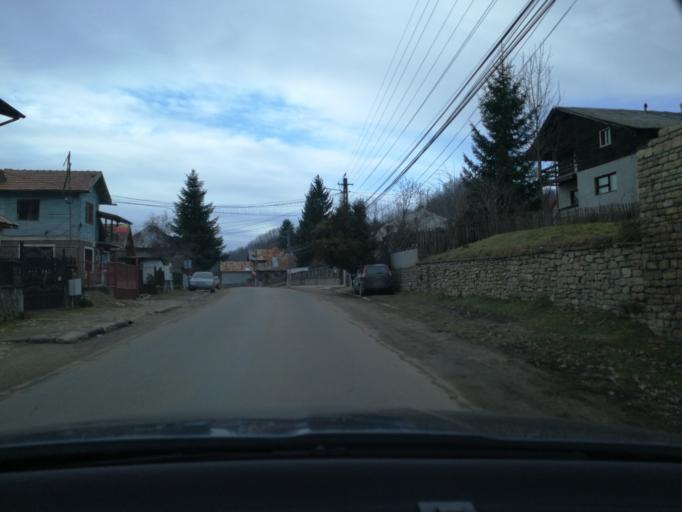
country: RO
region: Dambovita
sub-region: Comuna Bezdead
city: Bezdead
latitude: 45.1414
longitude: 25.4961
